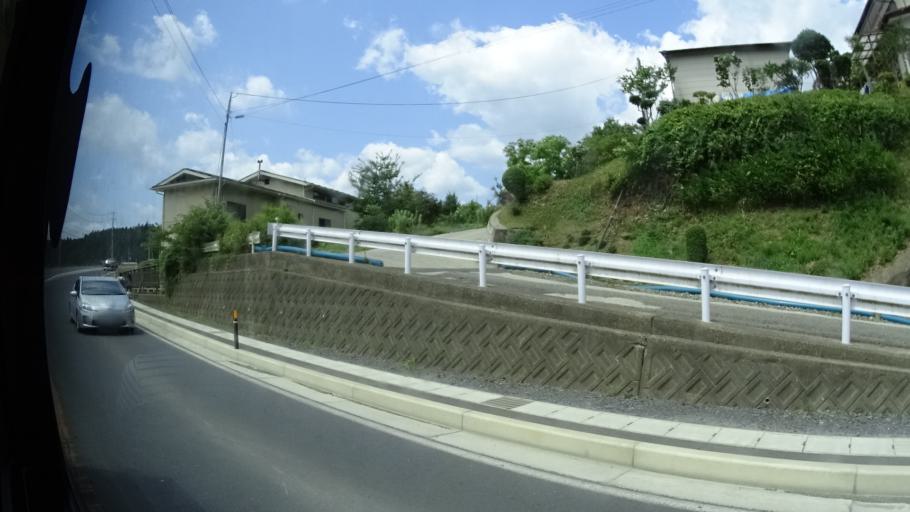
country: JP
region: Miyagi
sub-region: Oshika Gun
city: Onagawa Cho
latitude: 38.6867
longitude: 141.4557
